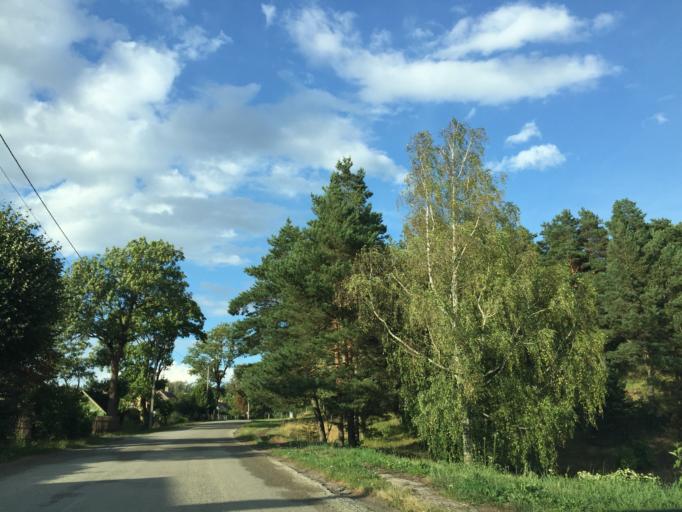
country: LT
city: Zagare
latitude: 56.3695
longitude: 23.2663
